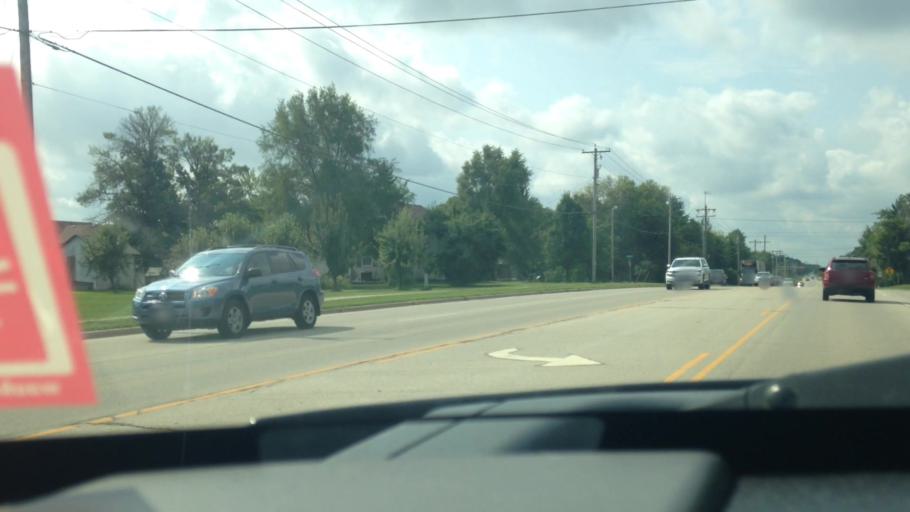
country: US
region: Wisconsin
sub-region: Waukesha County
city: Menomonee Falls
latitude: 43.1512
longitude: -88.1044
